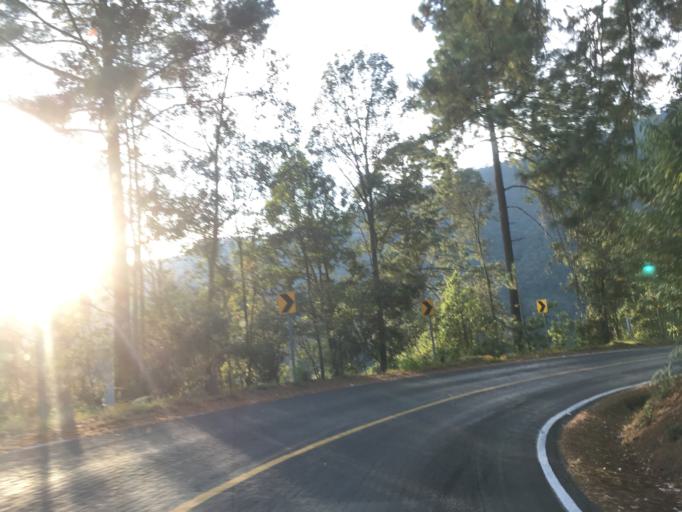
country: MX
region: Michoacan
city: Tzitzio
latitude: 19.6678
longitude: -100.9161
